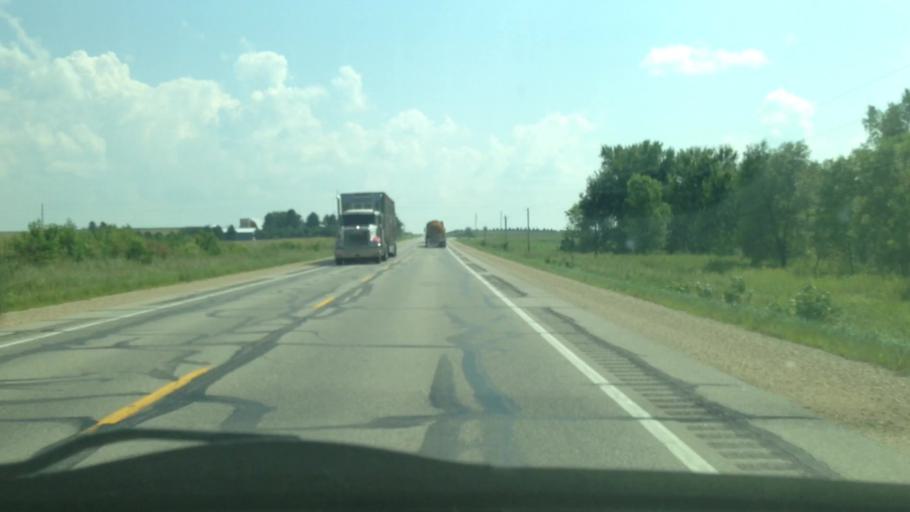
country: US
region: Iowa
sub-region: Chickasaw County
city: New Hampton
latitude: 43.2023
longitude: -92.2983
